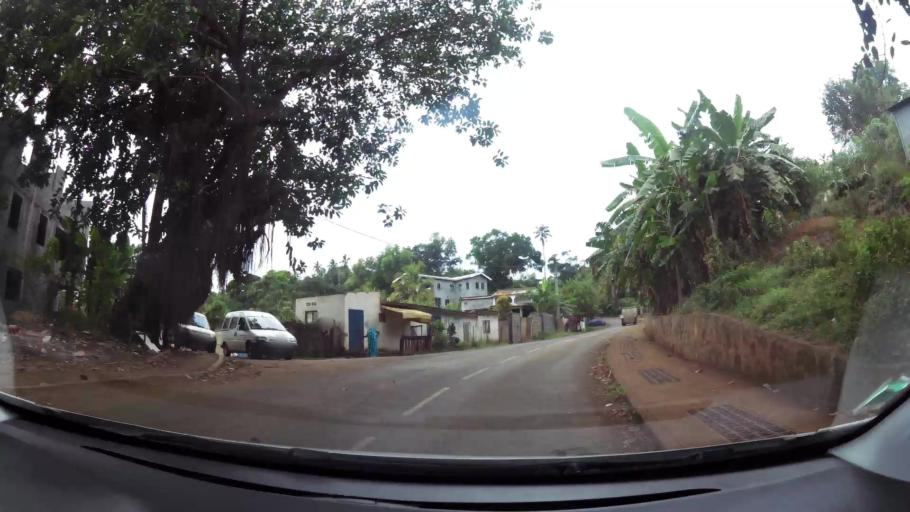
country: YT
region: Chiconi
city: Chiconi
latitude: -12.8328
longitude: 45.1189
